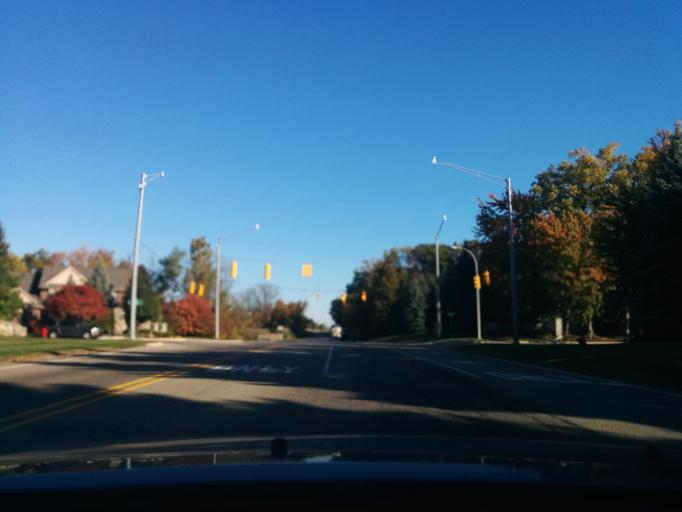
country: US
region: Michigan
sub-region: Oakland County
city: Novi
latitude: 42.4714
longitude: -83.5145
